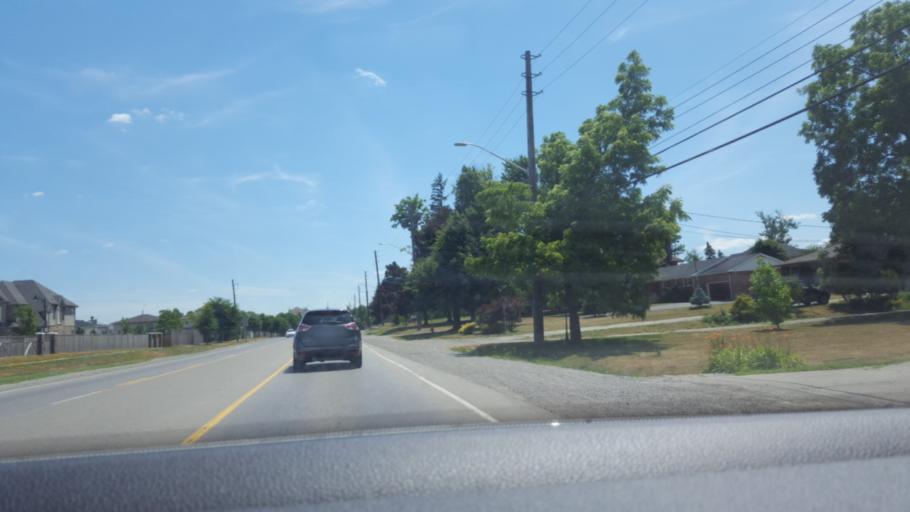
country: CA
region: Ontario
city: Hamilton
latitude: 43.2010
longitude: -79.8872
